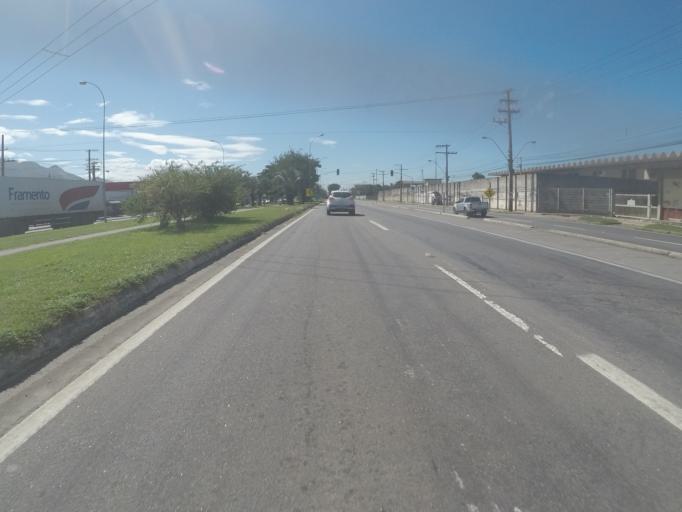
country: BR
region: Espirito Santo
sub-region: Serra
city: Serra
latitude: -20.2131
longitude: -40.2697
